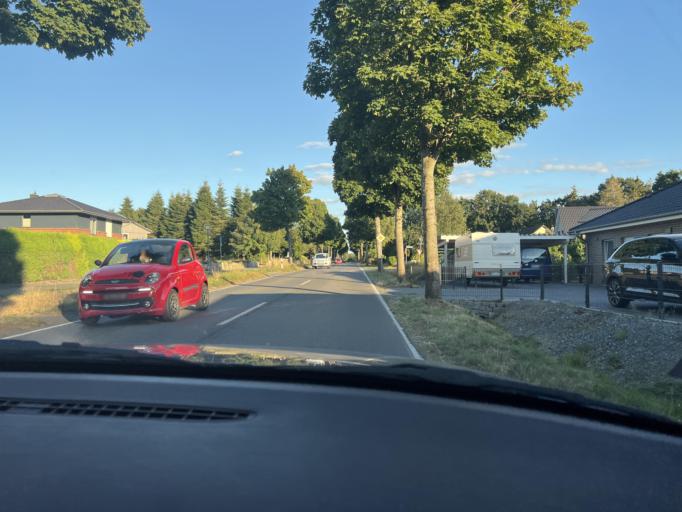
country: DE
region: Schleswig-Holstein
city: Hennstedt
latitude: 54.2862
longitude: 9.1551
